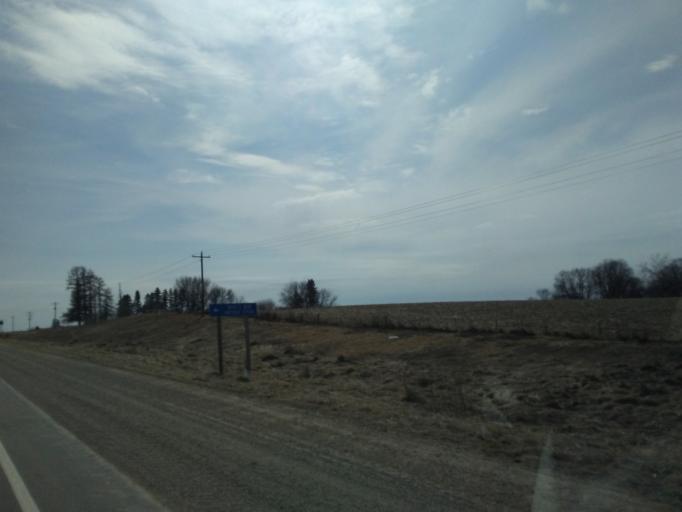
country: US
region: Iowa
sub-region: Winneshiek County
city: Decorah
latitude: 43.4451
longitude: -91.8623
